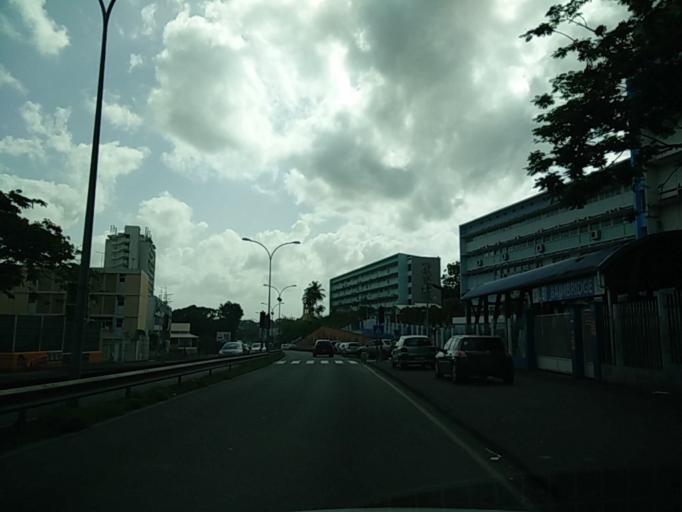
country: GP
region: Guadeloupe
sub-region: Guadeloupe
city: Pointe-a-Pitre
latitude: 16.2488
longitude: -61.5248
